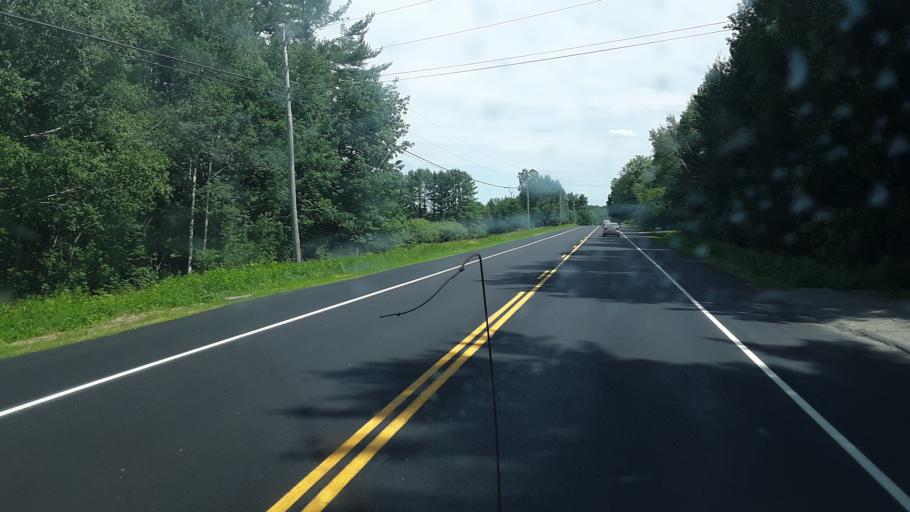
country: US
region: Maine
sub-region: Somerset County
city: Norridgewock
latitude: 44.6663
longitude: -69.7110
